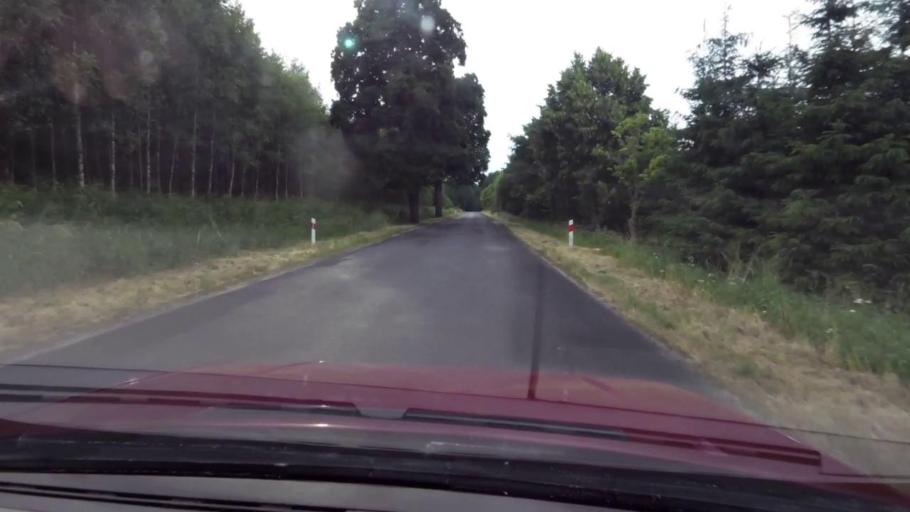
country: PL
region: Pomeranian Voivodeship
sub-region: Powiat bytowski
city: Trzebielino
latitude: 54.2680
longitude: 17.0283
